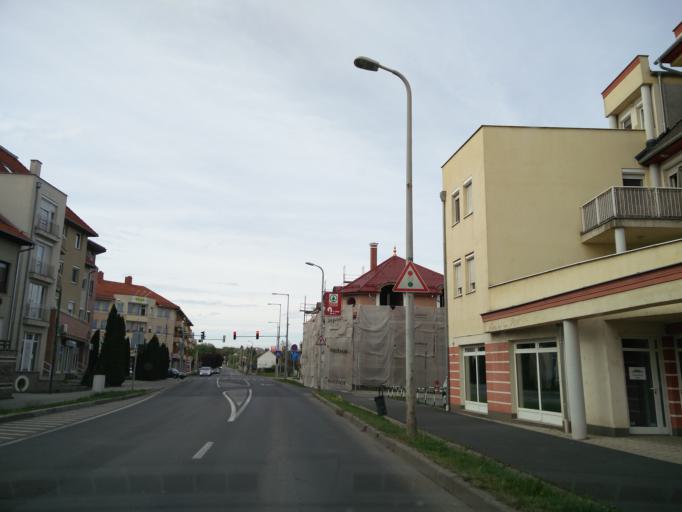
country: HU
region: Zala
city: Zalaegerszeg
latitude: 46.8469
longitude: 16.8466
